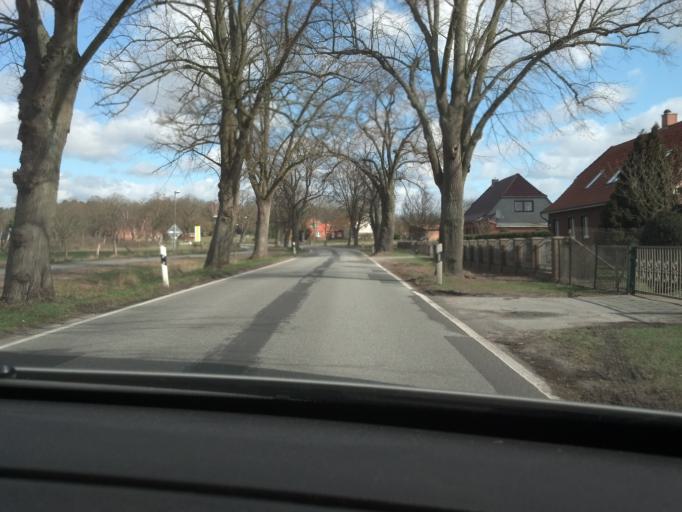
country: DE
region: Mecklenburg-Vorpommern
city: Boizenburg
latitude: 53.4001
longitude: 10.7491
